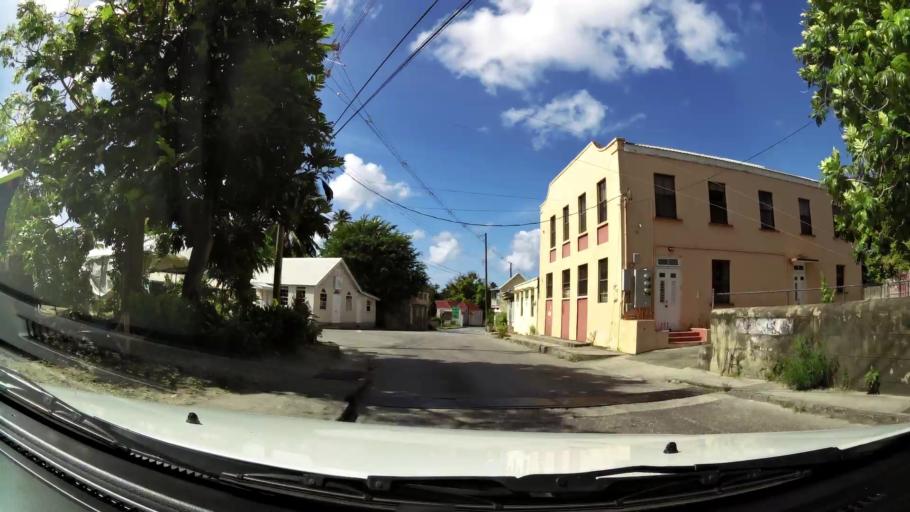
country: BB
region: Saint Peter
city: Speightstown
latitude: 13.2523
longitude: -59.6397
